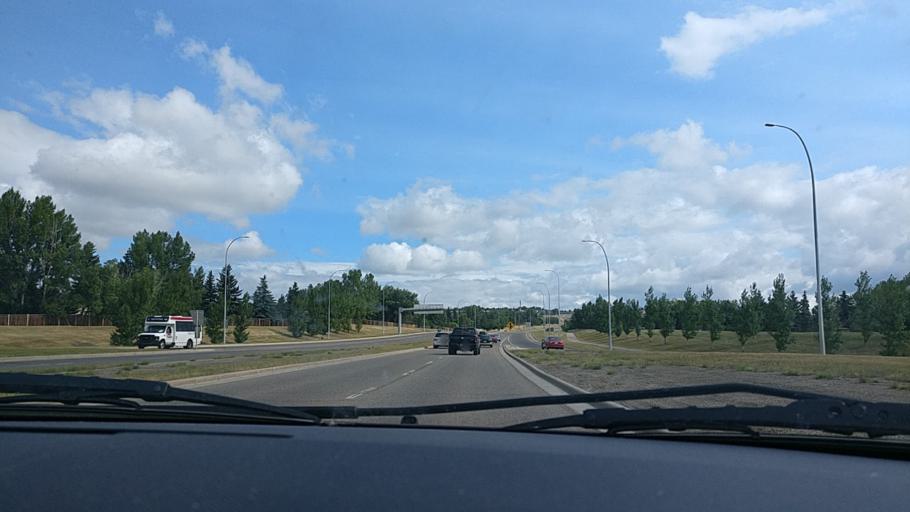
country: CA
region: Alberta
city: Calgary
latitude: 51.1117
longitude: -114.1774
